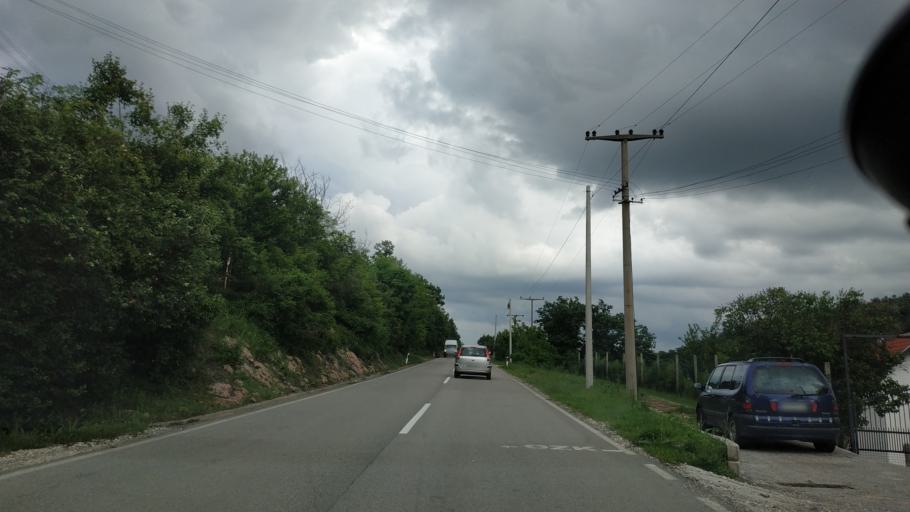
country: RS
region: Central Serbia
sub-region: Borski Okrug
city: Bor
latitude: 44.0504
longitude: 22.0739
